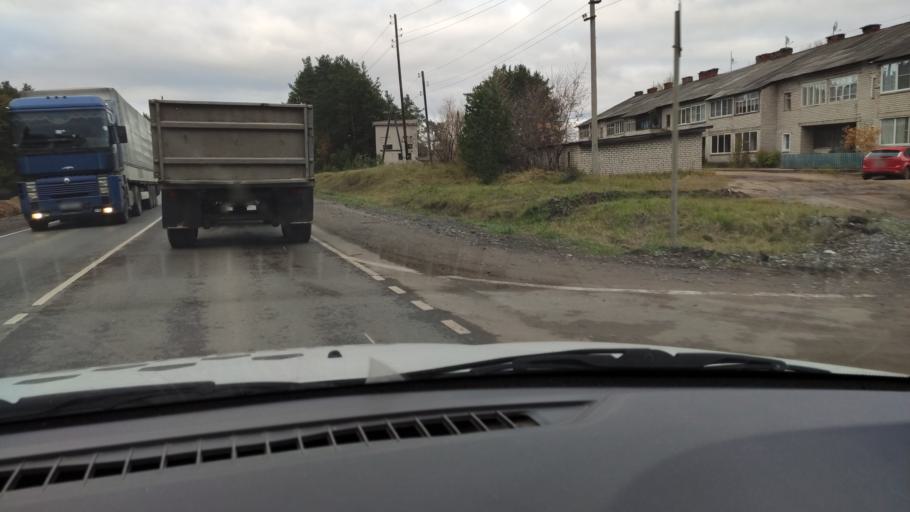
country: RU
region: Kirov
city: Belaya Kholunitsa
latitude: 58.8502
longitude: 50.8285
